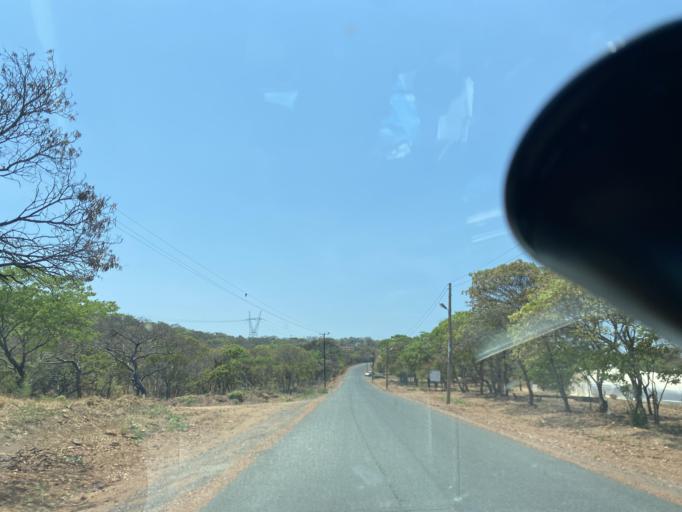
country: ZM
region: Lusaka
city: Kafue
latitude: -15.8662
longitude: 28.4472
